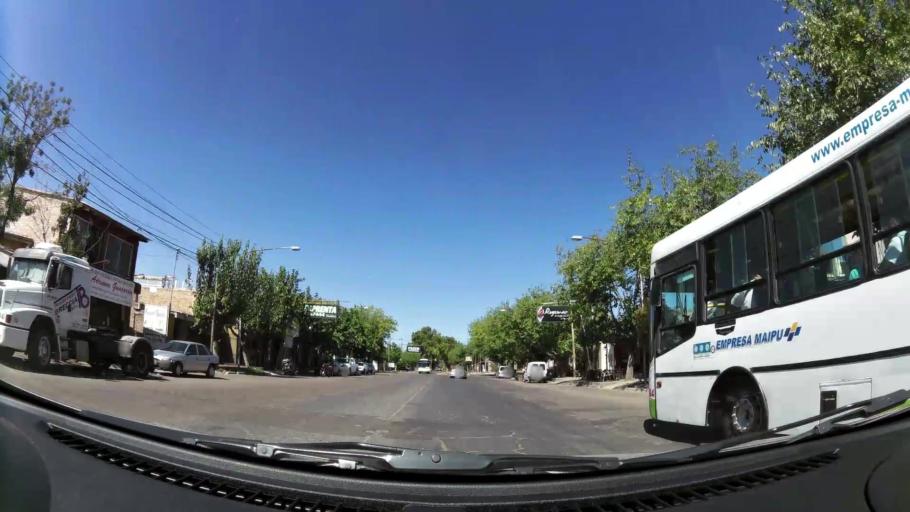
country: AR
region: Mendoza
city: Villa Nueva
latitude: -32.8958
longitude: -68.7802
